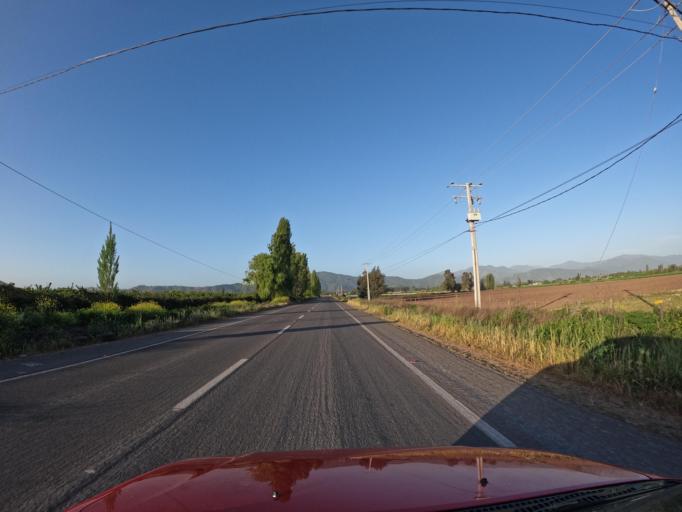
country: CL
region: O'Higgins
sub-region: Provincia de Cachapoal
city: San Vicente
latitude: -34.2986
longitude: -71.3734
